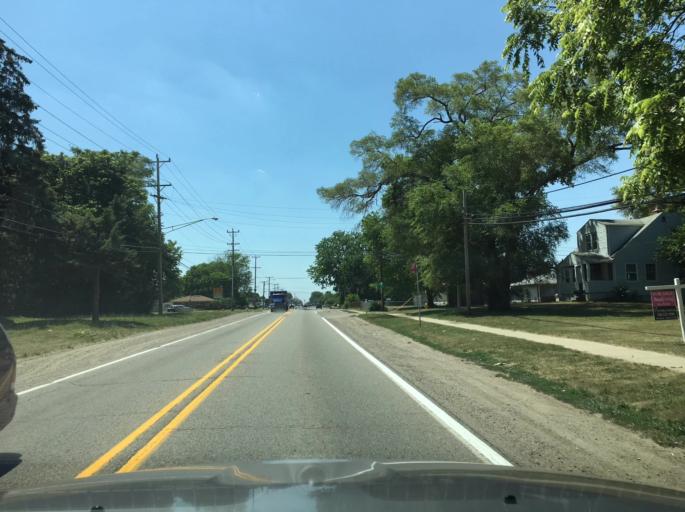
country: US
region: Michigan
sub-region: Macomb County
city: Clinton
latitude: 42.5548
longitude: -82.8927
